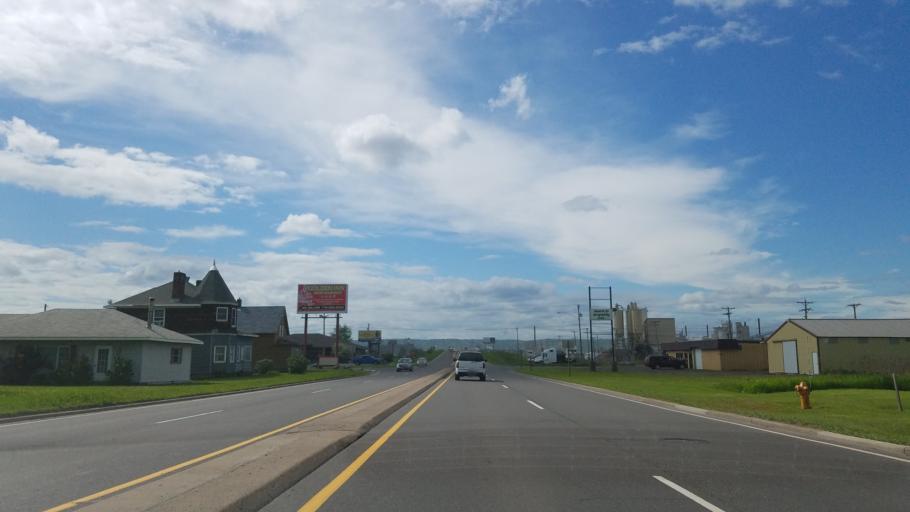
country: US
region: Wisconsin
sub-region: Douglas County
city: Superior
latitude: 46.7247
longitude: -92.0719
